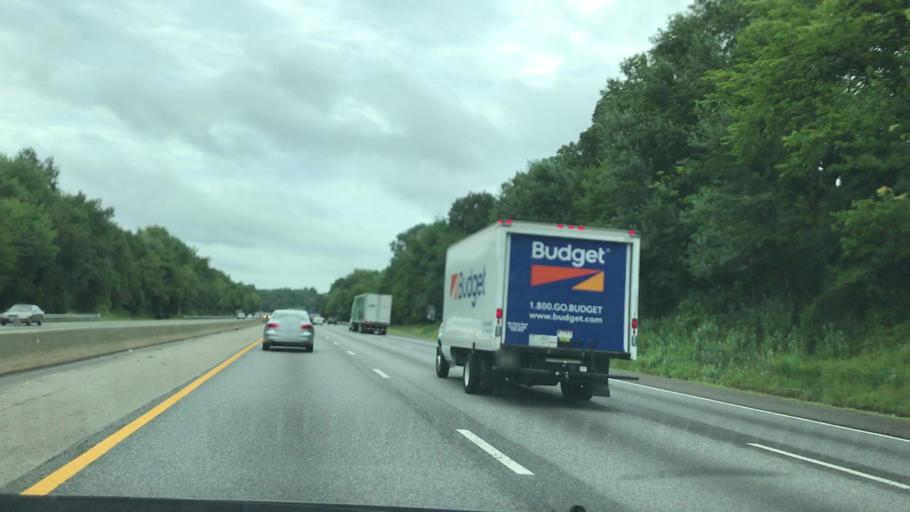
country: US
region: Virginia
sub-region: City of Colonial Heights
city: Colonial Heights
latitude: 37.2718
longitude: -77.3932
